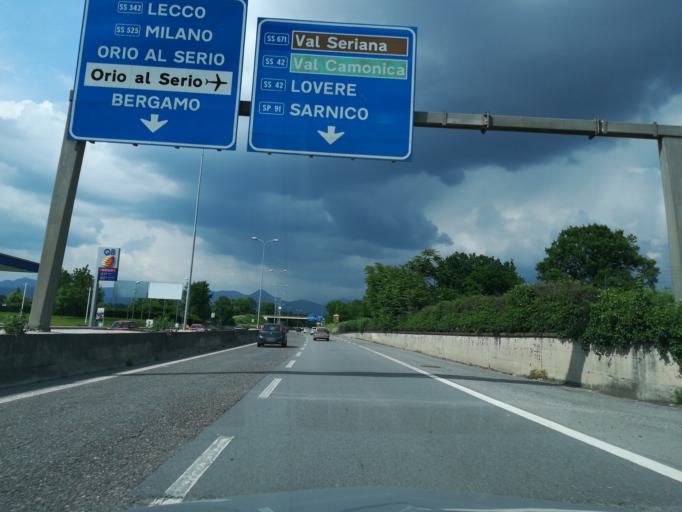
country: IT
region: Lombardy
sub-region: Provincia di Bergamo
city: Grassobbio
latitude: 45.6611
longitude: 9.7370
